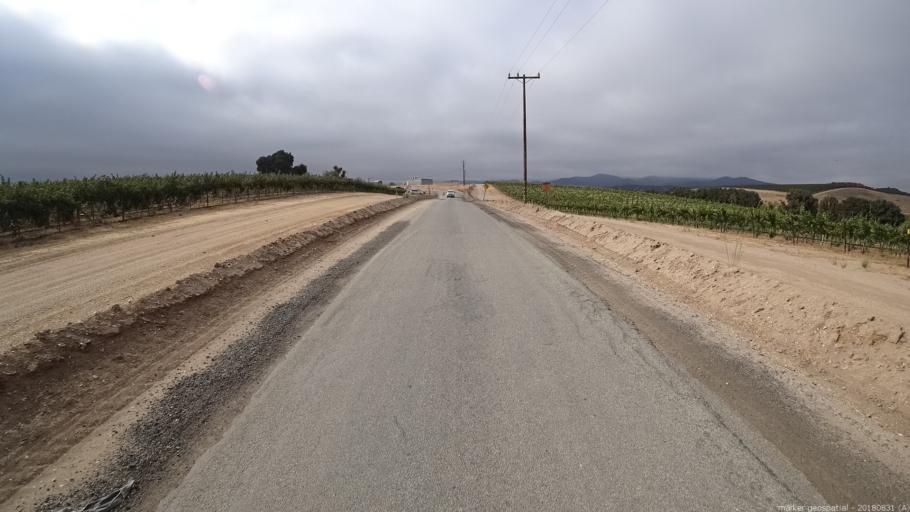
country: US
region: California
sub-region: Monterey County
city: King City
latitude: 36.1347
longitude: -121.0923
